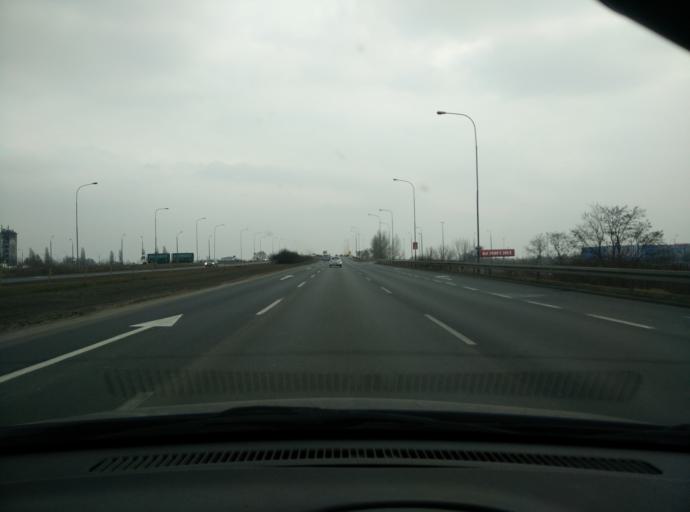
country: PL
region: Greater Poland Voivodeship
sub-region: Poznan
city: Poznan
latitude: 52.3773
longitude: 16.9806
